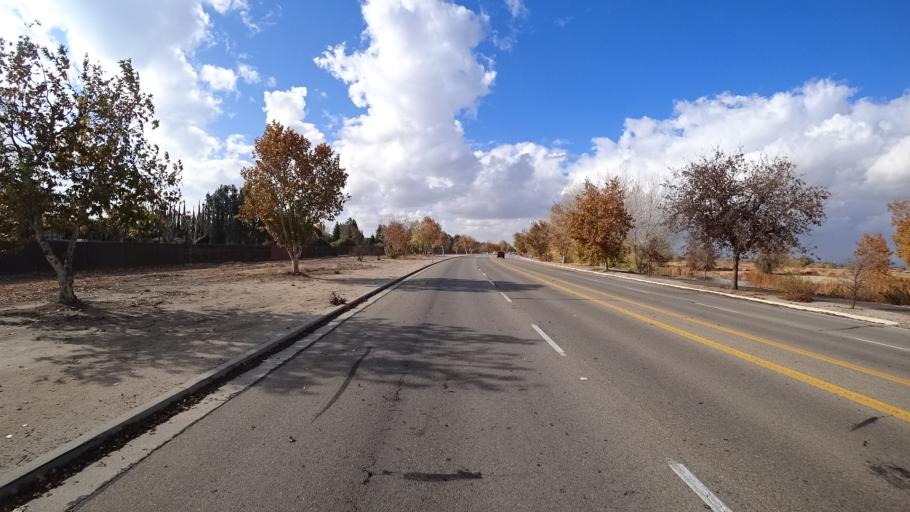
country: US
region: California
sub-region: Kern County
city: Greenacres
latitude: 35.3613
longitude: -119.0793
